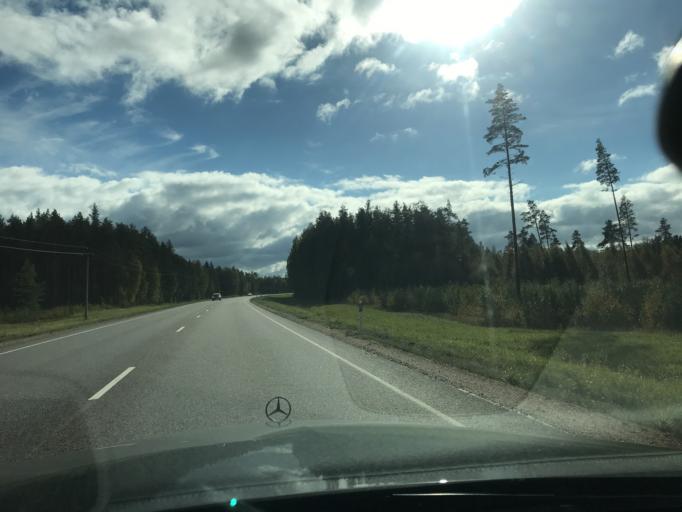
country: EE
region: Vorumaa
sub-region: Voru linn
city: Voru
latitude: 57.8384
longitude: 27.0565
